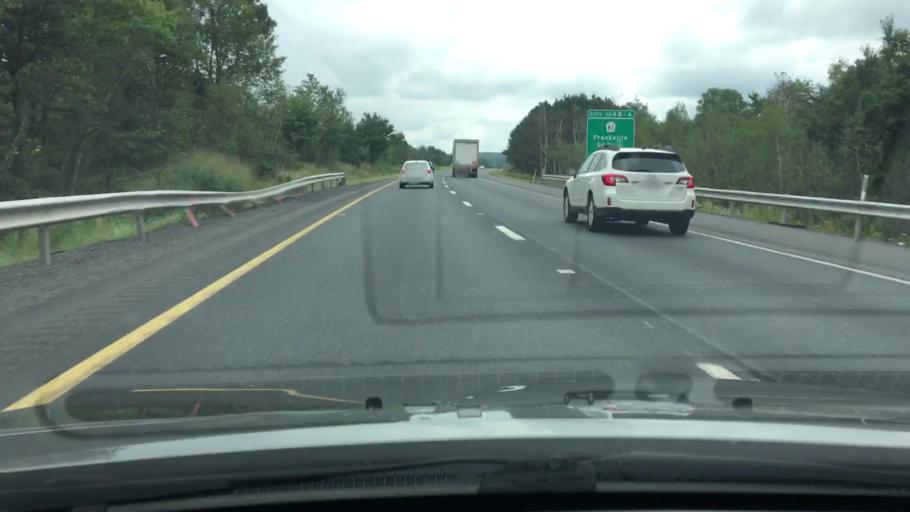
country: US
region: Pennsylvania
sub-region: Schuylkill County
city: Frackville
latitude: 40.7749
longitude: -76.2015
